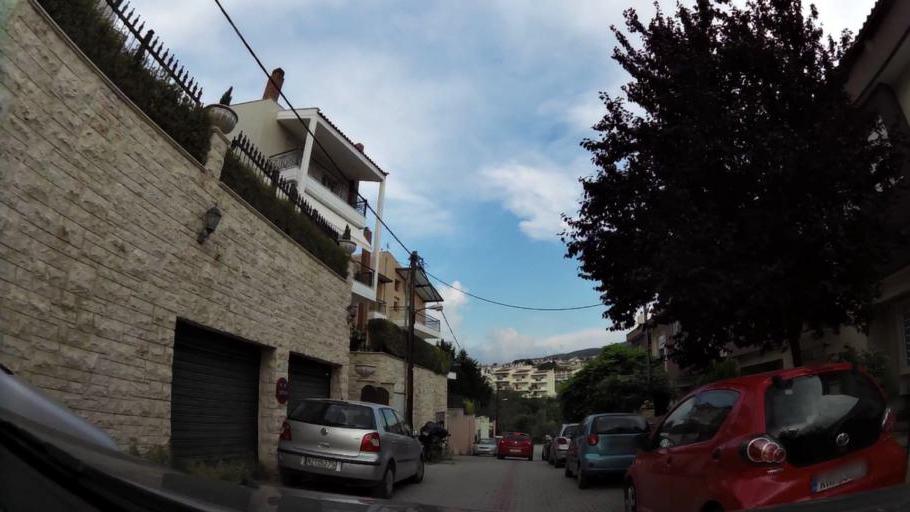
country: GR
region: Central Macedonia
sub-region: Nomos Thessalonikis
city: Pefka
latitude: 40.6620
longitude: 22.9765
